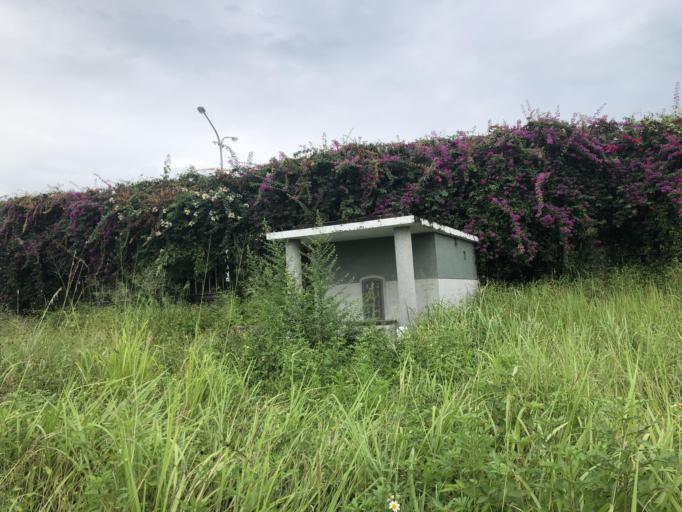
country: TW
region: Taiwan
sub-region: Tainan
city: Tainan
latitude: 22.9654
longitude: 120.1981
